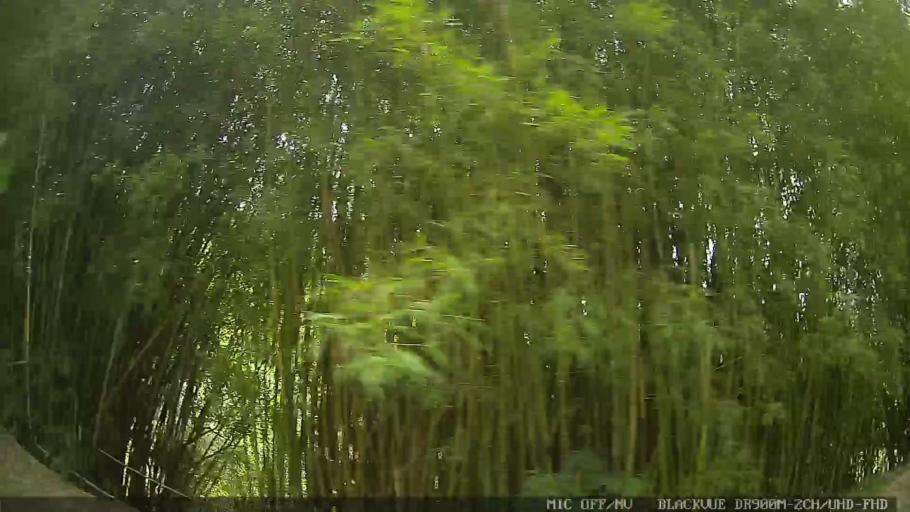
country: BR
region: Sao Paulo
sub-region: Santa Branca
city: Santa Branca
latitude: -23.5251
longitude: -45.8046
